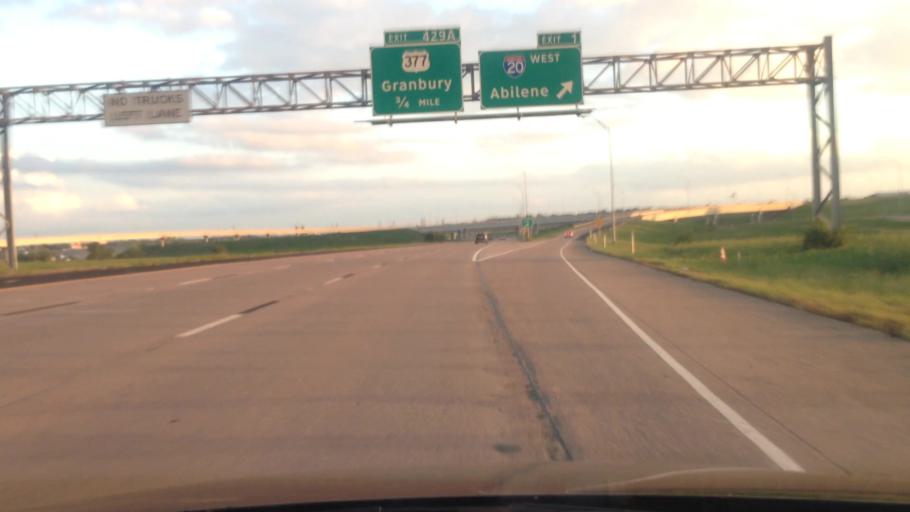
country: US
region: Texas
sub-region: Tarrant County
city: Benbrook
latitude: 32.7003
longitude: -97.4728
